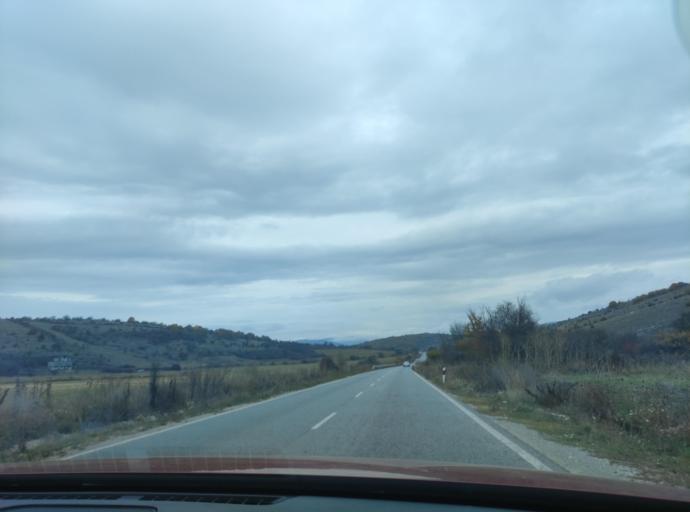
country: BG
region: Sofiya
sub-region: Obshtina Godech
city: Godech
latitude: 42.9533
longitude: 23.1574
